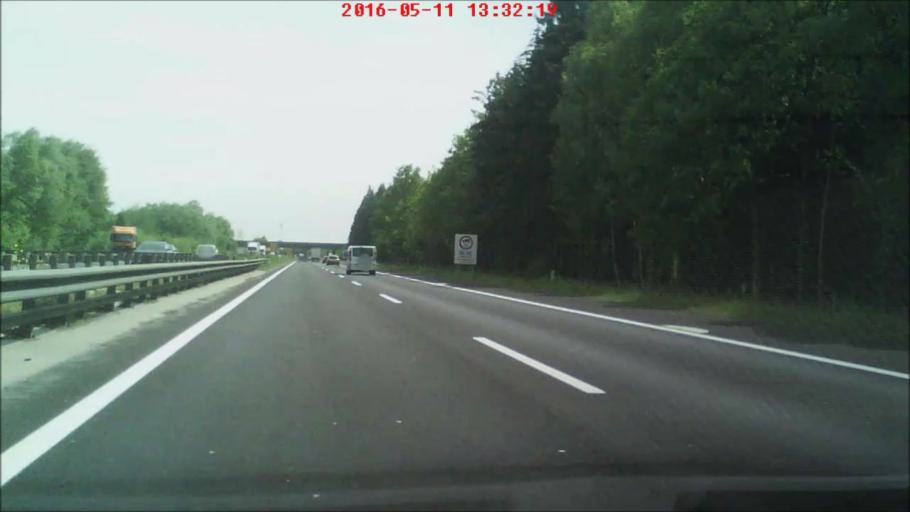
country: AT
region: Upper Austria
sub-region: Politischer Bezirk Scharding
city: Sankt Marienkirchen bei Schaerding
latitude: 48.3240
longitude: 13.4148
